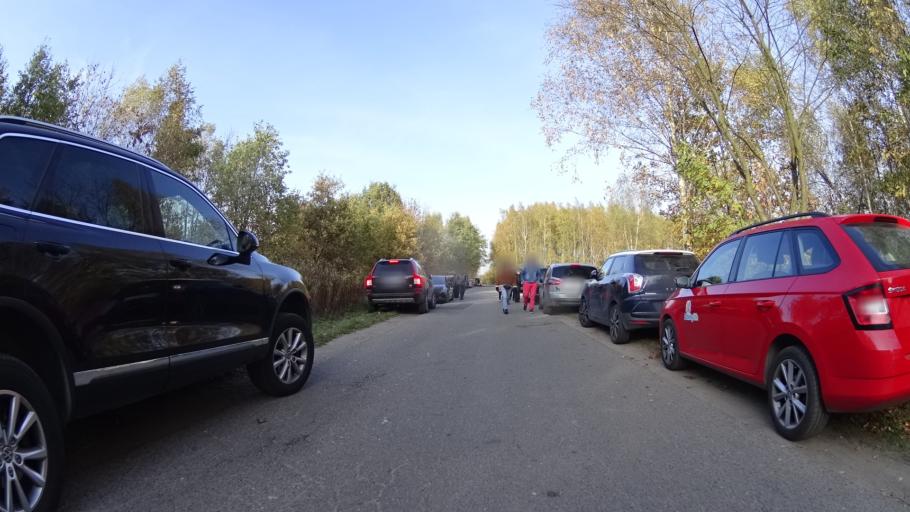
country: PL
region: Masovian Voivodeship
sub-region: Powiat warszawski zachodni
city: Lomianki
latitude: 52.2954
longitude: 20.8891
